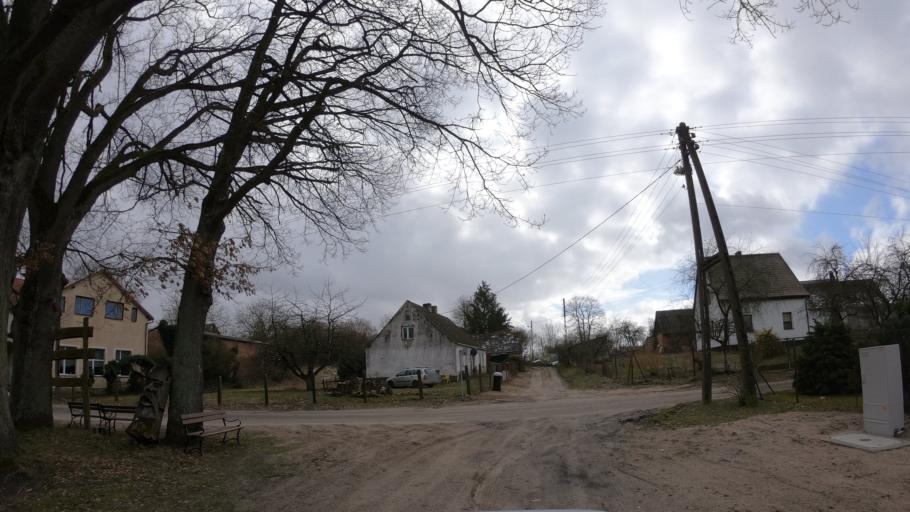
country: PL
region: West Pomeranian Voivodeship
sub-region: Powiat kamienski
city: Miedzyzdroje
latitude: 53.9316
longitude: 14.5470
